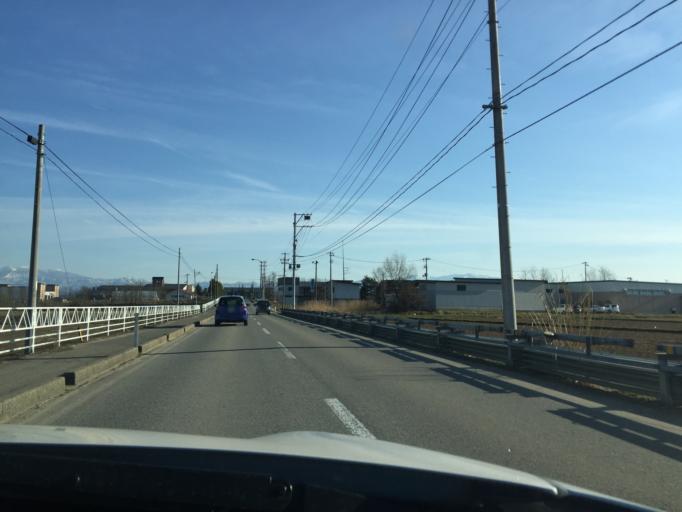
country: JP
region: Yamagata
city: Nagai
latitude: 38.0168
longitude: 140.0555
